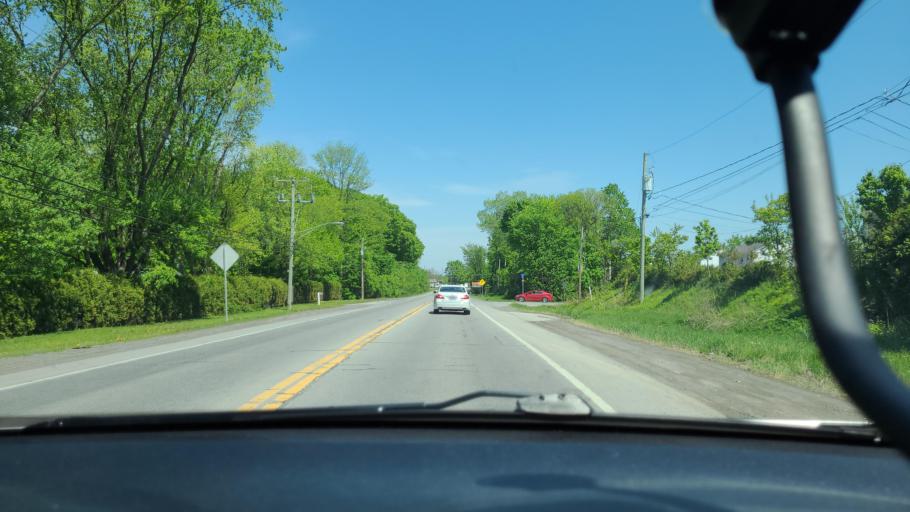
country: CA
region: Quebec
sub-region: Laurentides
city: Saint-Eustache
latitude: 45.5864
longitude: -73.9359
